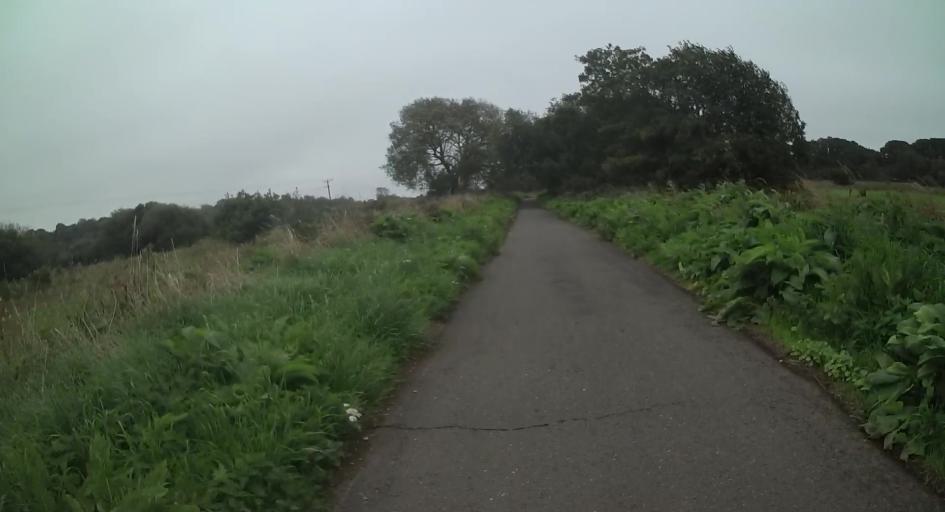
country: GB
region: England
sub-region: Isle of Wight
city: Sandown
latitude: 50.6664
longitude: -1.1821
